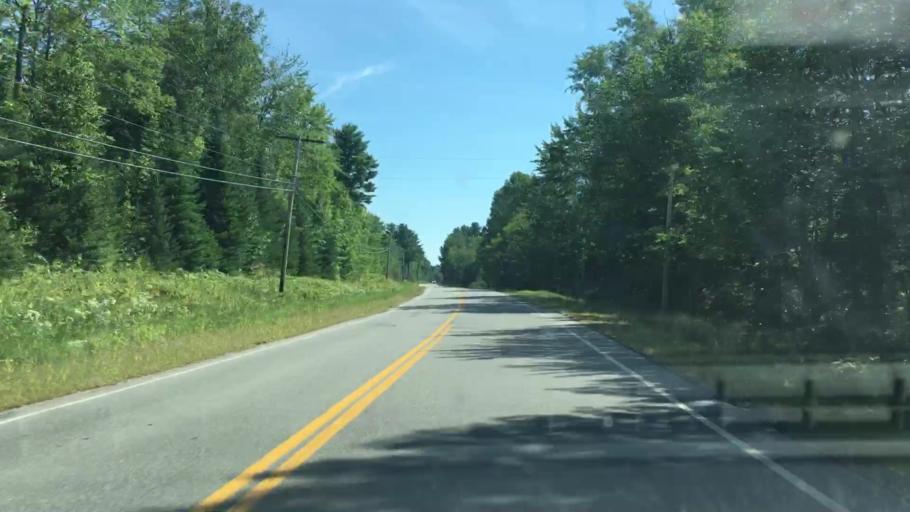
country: US
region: Maine
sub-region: Piscataquis County
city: Milo
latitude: 45.1954
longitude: -68.9025
